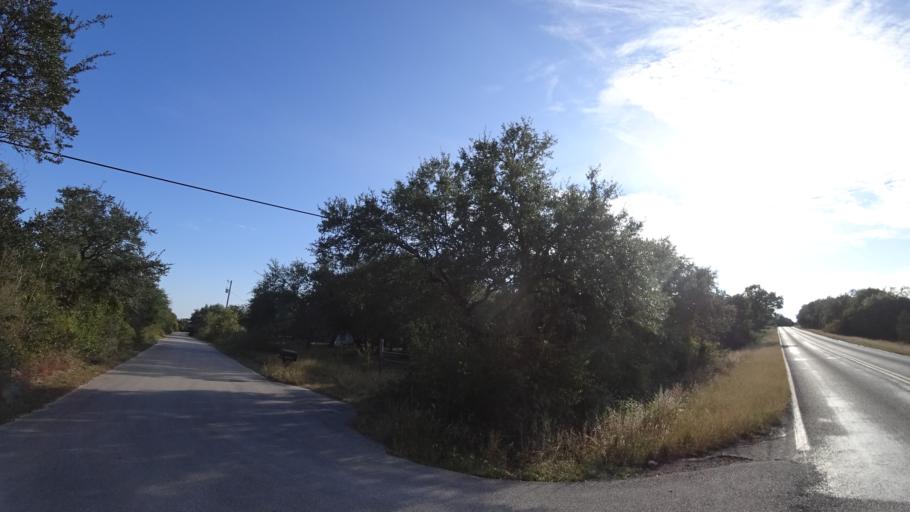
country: US
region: Texas
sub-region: Travis County
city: Bee Cave
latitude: 30.2435
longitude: -97.9369
